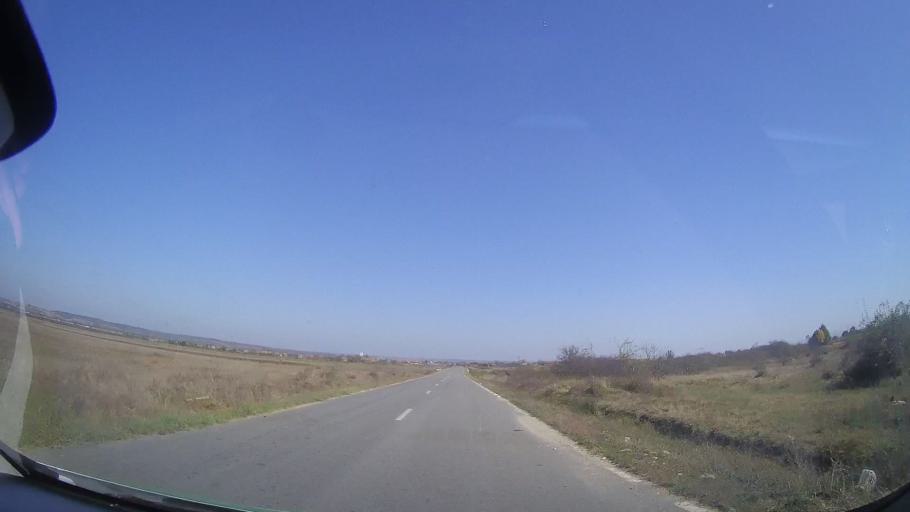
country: RO
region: Timis
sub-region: Comuna Bethausen
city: Bethausen
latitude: 45.7956
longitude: 21.9860
